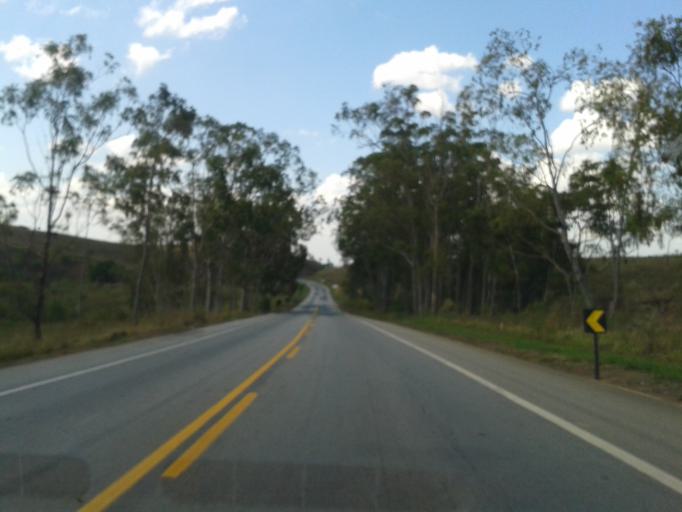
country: BR
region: Minas Gerais
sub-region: Campos Altos
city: Campos Altos
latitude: -19.7144
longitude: -45.9277
